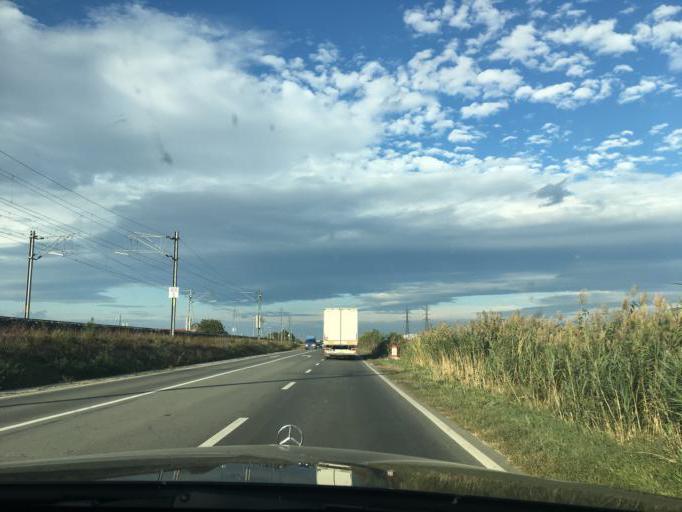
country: RO
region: Alba
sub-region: Municipiul Alba Iulia
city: Alba Iulia
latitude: 46.0676
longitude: 23.5928
